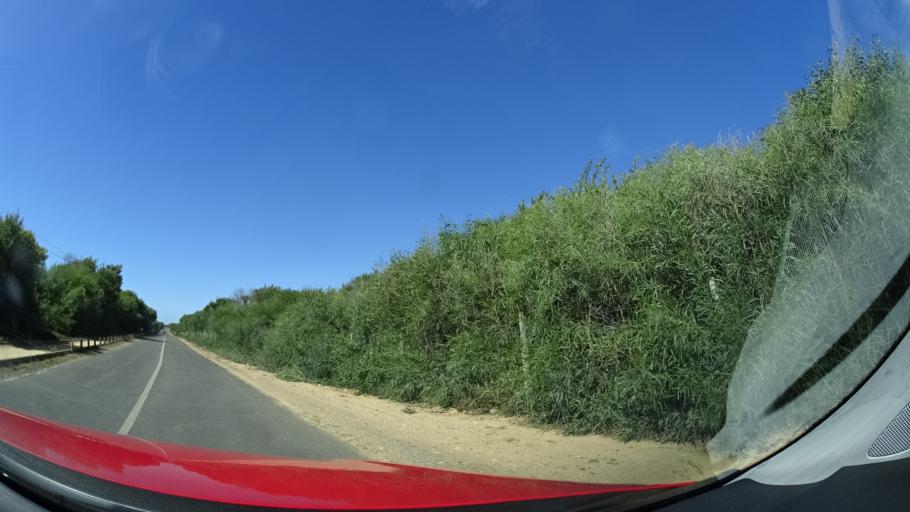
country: PT
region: Beja
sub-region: Odemira
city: Sao Teotonio
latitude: 37.5357
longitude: -8.7847
